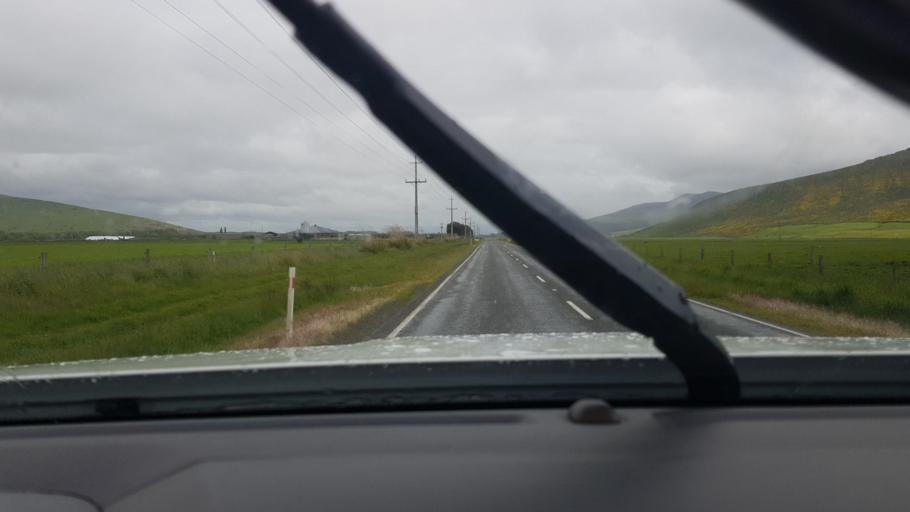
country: NZ
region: Southland
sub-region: Southland District
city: Winton
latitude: -45.7792
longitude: 168.3978
